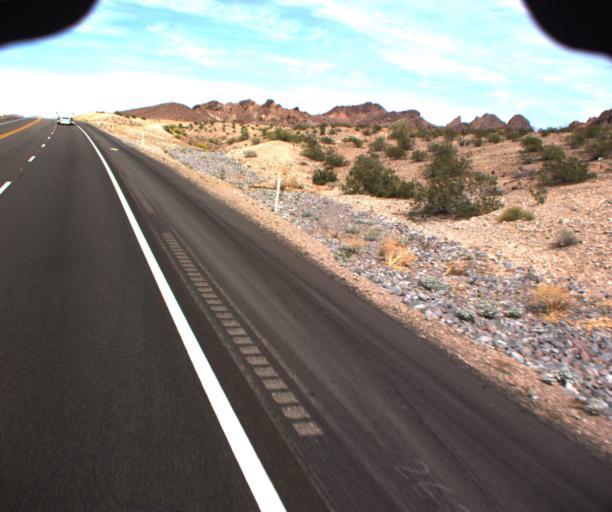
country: US
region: Arizona
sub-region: Mohave County
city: Desert Hills
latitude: 34.6261
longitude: -114.3323
